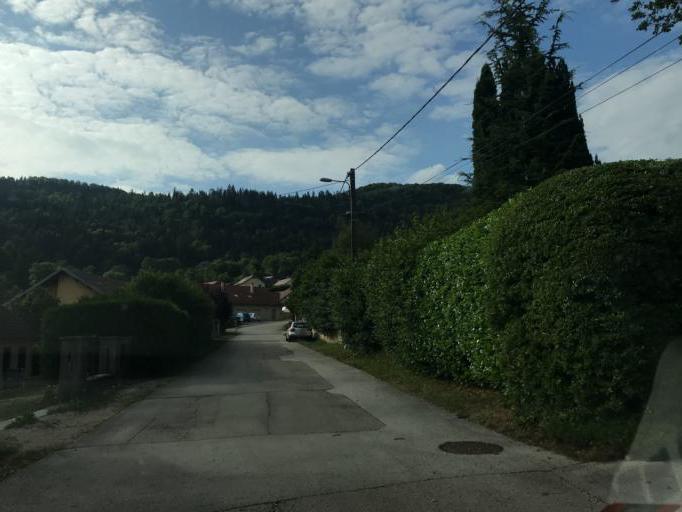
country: FR
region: Franche-Comte
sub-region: Departement du Jura
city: Saint-Lupicin
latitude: 46.4258
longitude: 5.8014
